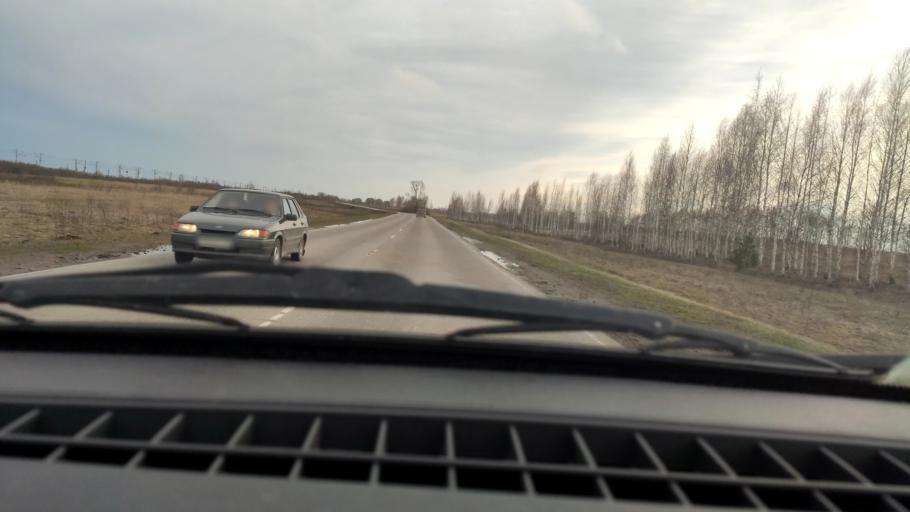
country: RU
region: Bashkortostan
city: Chishmy
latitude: 54.4366
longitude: 55.2369
